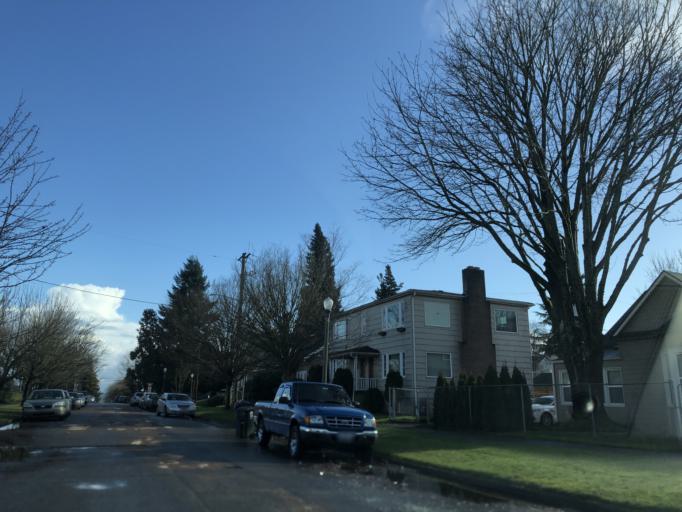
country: US
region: Washington
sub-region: Pierce County
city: Tacoma
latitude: 47.2559
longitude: -122.4555
